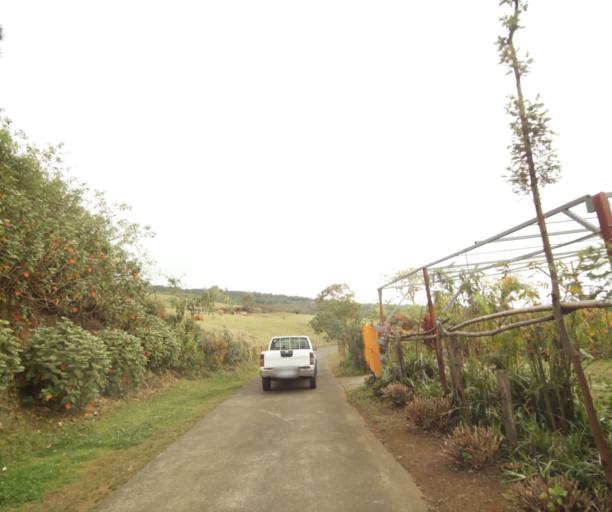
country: RE
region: Reunion
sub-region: Reunion
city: Saint-Paul
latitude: -21.0164
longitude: 55.3501
